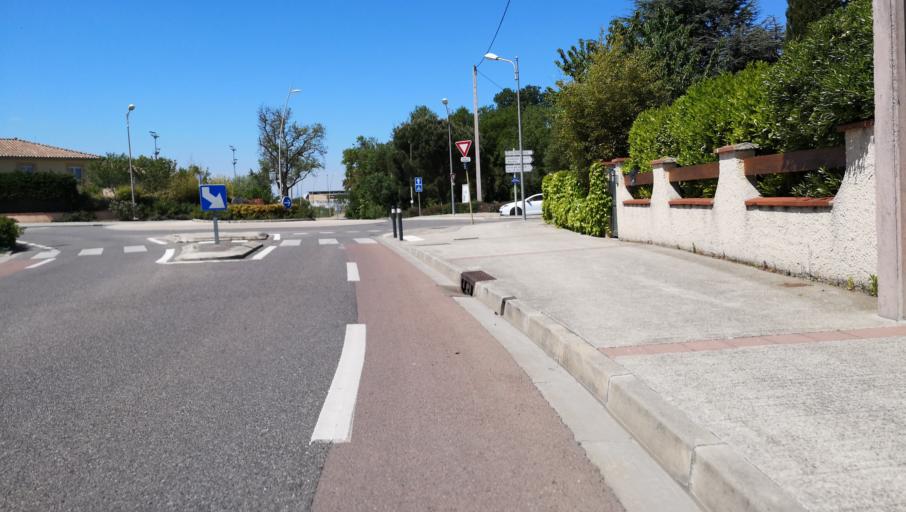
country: FR
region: Midi-Pyrenees
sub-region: Departement de la Haute-Garonne
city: Beauzelle
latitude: 43.6509
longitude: 1.3855
